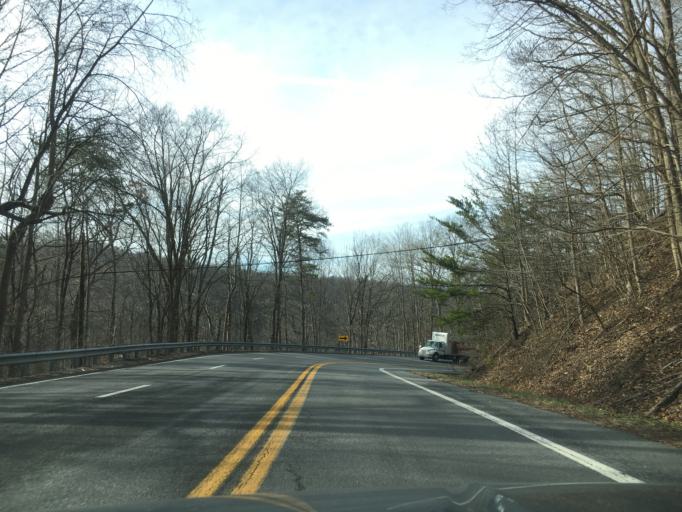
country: US
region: West Virginia
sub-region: Fayette County
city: Ansted
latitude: 38.1311
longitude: -81.1451
